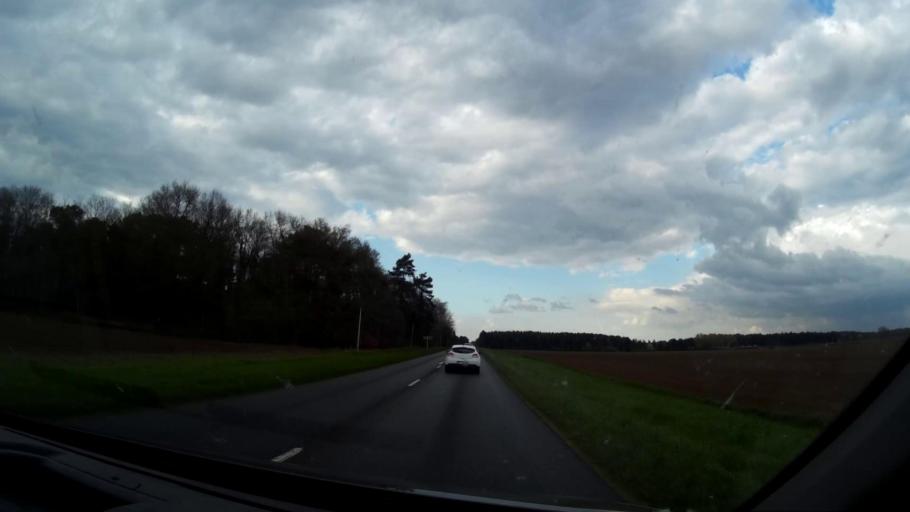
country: FR
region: Centre
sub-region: Departement du Loir-et-Cher
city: Contres
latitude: 47.4498
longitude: 1.4261
